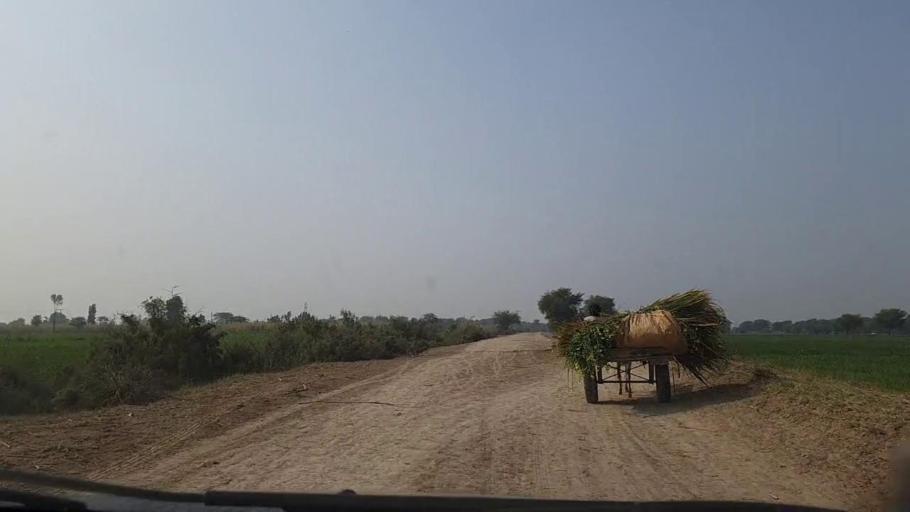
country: PK
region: Sindh
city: Sanghar
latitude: 26.0345
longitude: 68.9833
